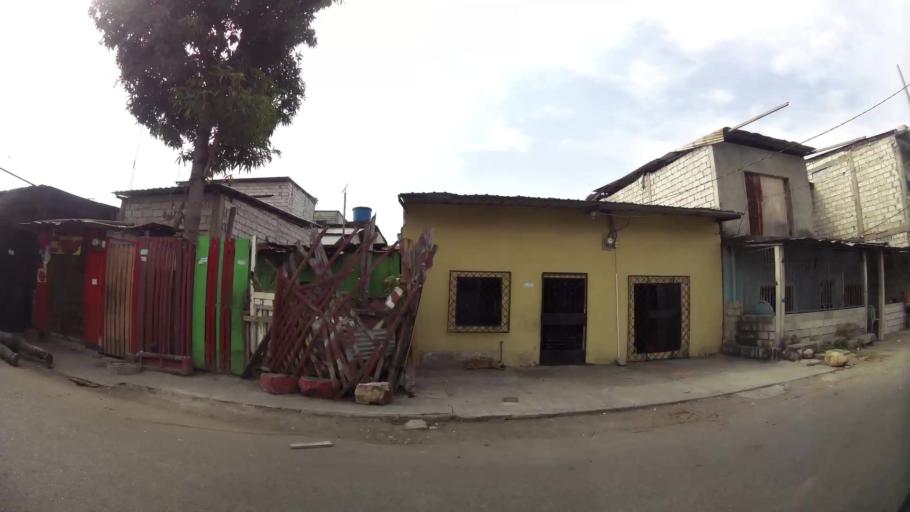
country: EC
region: Guayas
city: Guayaquil
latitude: -2.2573
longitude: -79.9064
